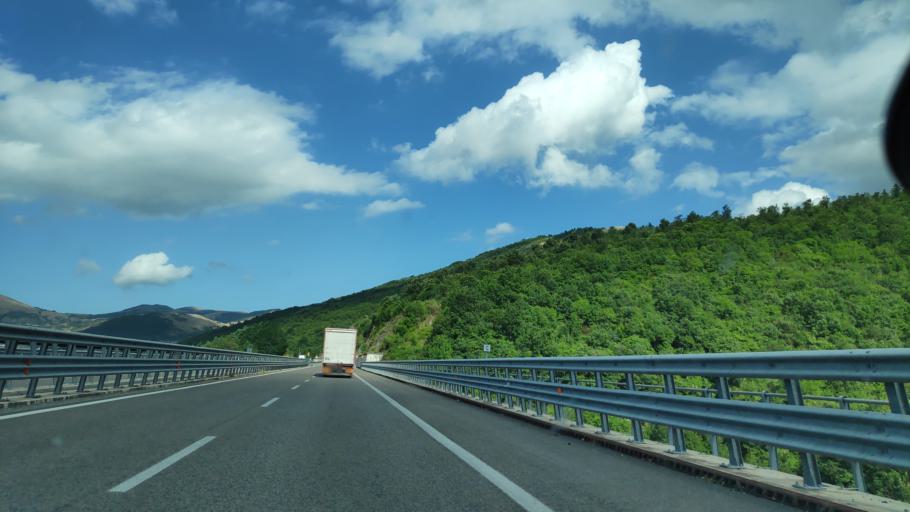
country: IT
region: Campania
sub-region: Provincia di Salerno
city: Pertosa
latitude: 40.5313
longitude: 15.4452
